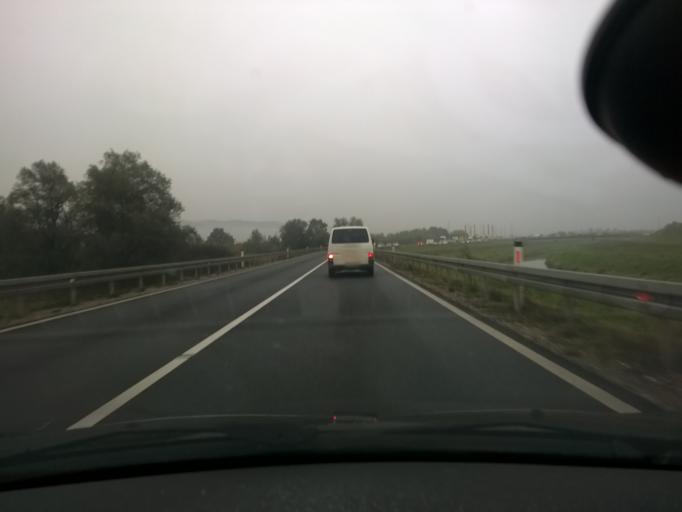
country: HR
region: Zagrebacka
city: Zapresic
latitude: 45.8822
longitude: 15.8196
